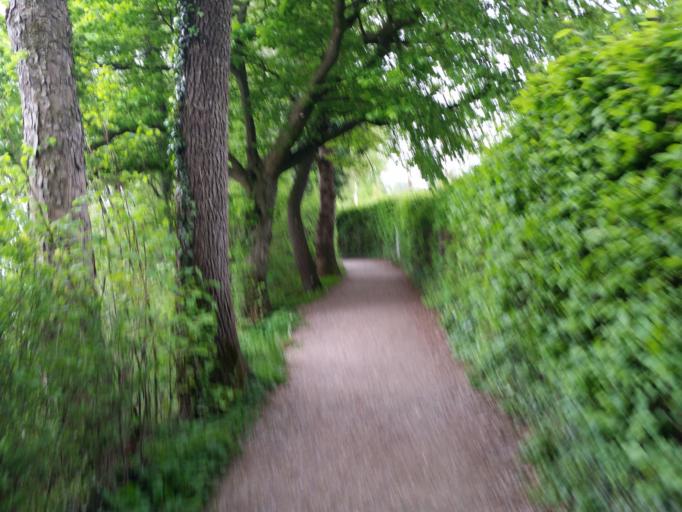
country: CH
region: Thurgau
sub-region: Arbon District
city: Uttwil
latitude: 47.5918
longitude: 9.3300
